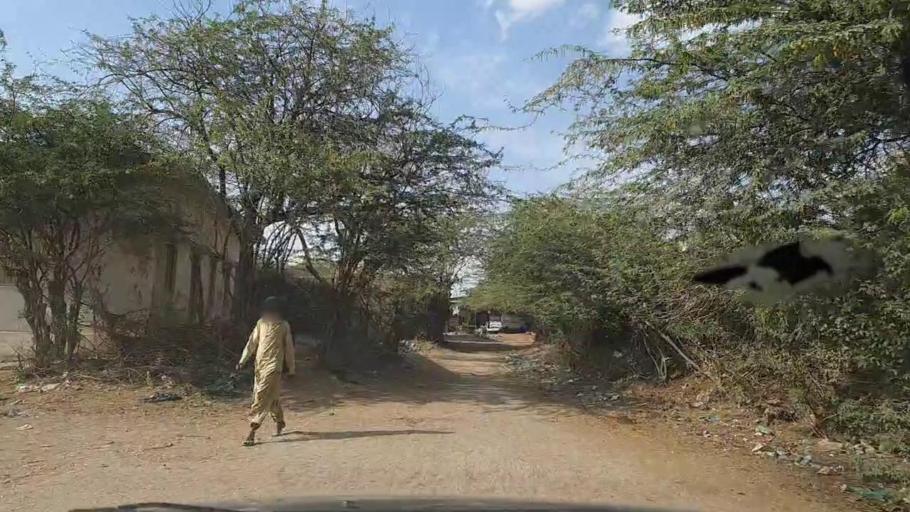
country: PK
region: Sindh
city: Daro Mehar
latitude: 24.8153
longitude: 68.0731
